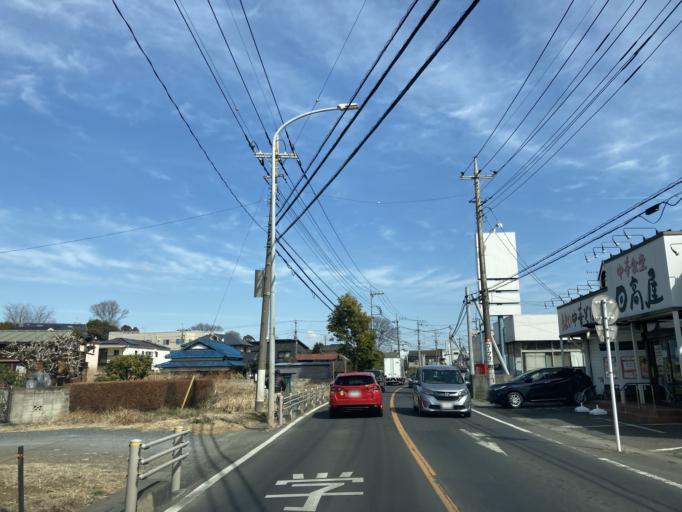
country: JP
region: Saitama
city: Tokorozawa
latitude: 35.8119
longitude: 139.4803
